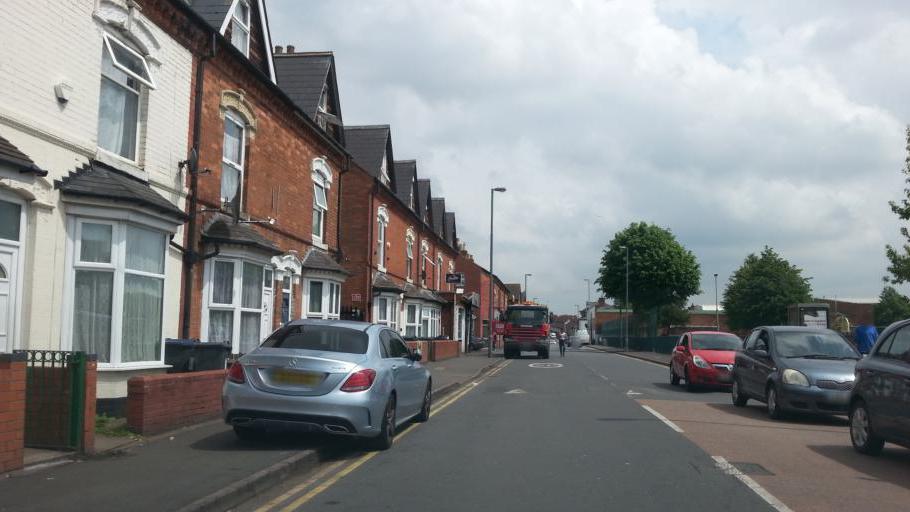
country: GB
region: England
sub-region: City and Borough of Birmingham
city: Birmingham
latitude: 52.4530
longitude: -1.8778
